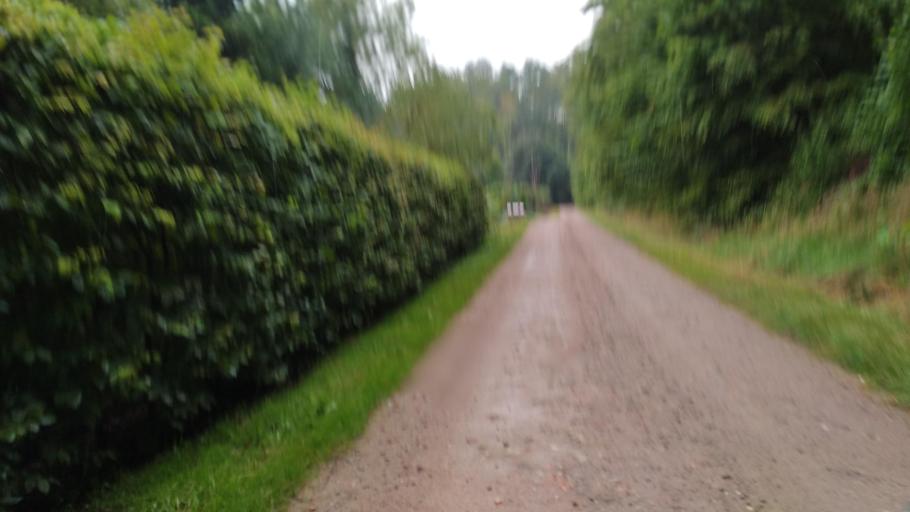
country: PL
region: Pomeranian Voivodeship
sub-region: Powiat wejherowski
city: Goscicino
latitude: 54.6340
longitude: 18.1328
